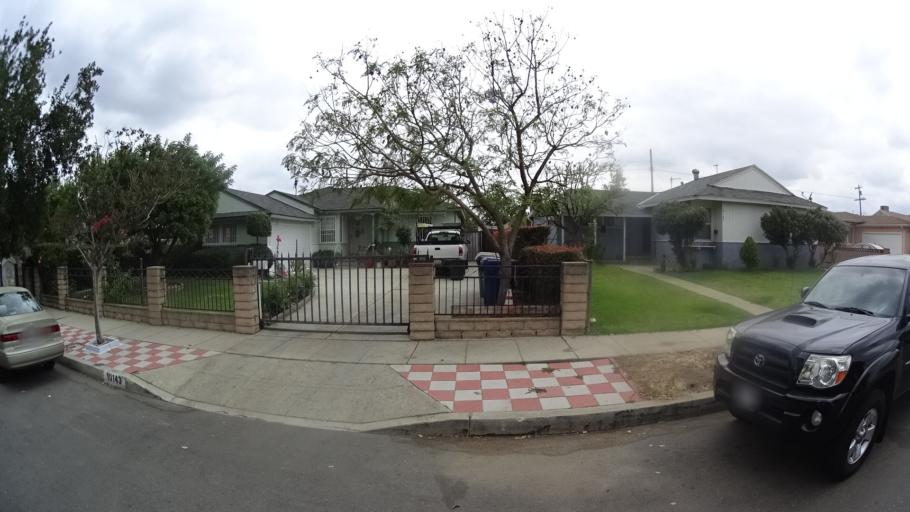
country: US
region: California
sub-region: Los Angeles County
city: San Fernando
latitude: 34.2551
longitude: -118.4413
